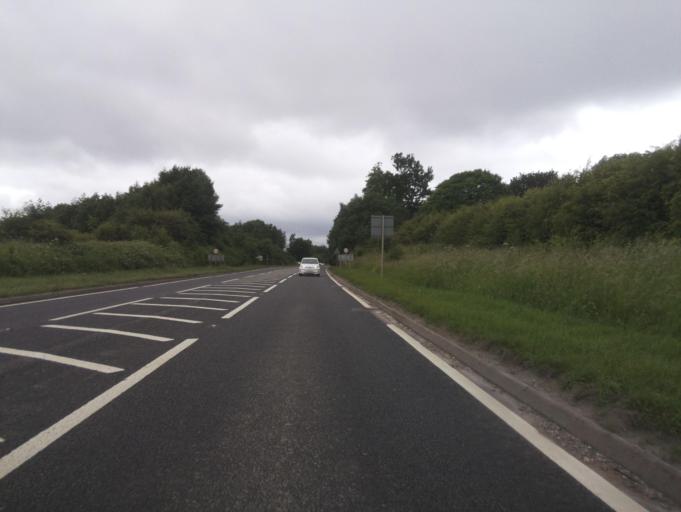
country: GB
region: England
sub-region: Leicestershire
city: Coalville
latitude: 52.7338
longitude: -1.4147
